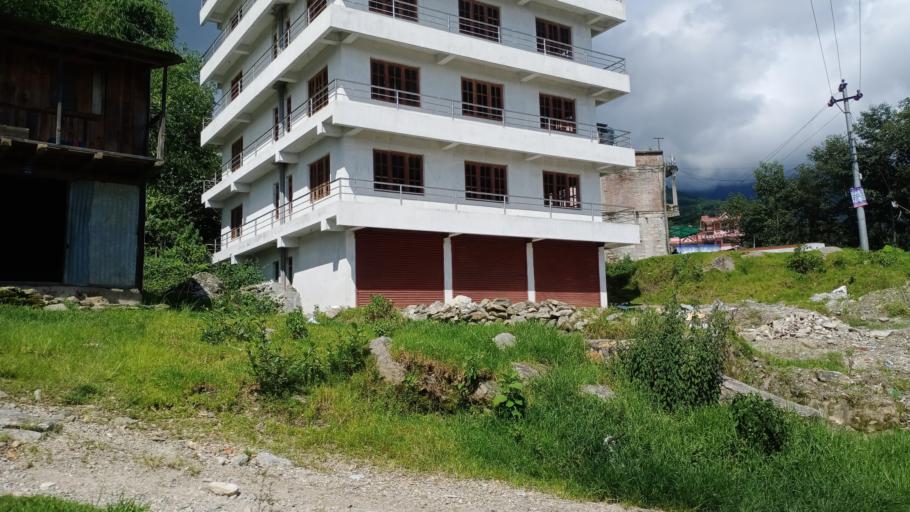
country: NP
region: Central Region
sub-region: Janakpur Zone
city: Ramechhap
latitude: 27.6488
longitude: 86.1394
